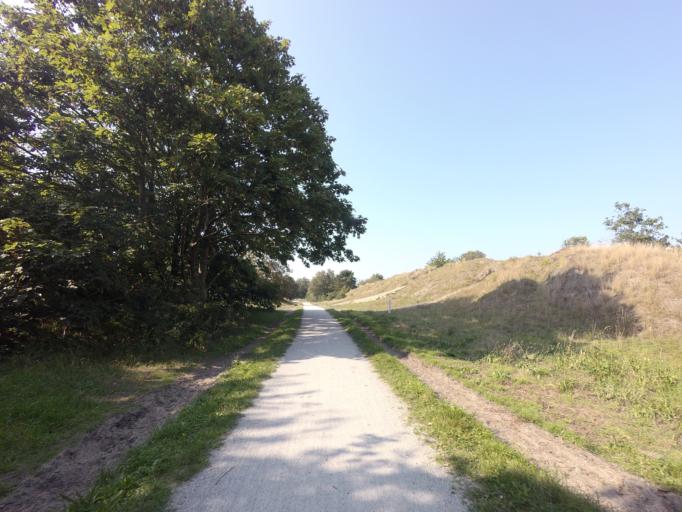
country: NL
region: Friesland
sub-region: Gemeente Schiermonnikoog
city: Schiermonnikoog
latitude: 53.4838
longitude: 6.1798
